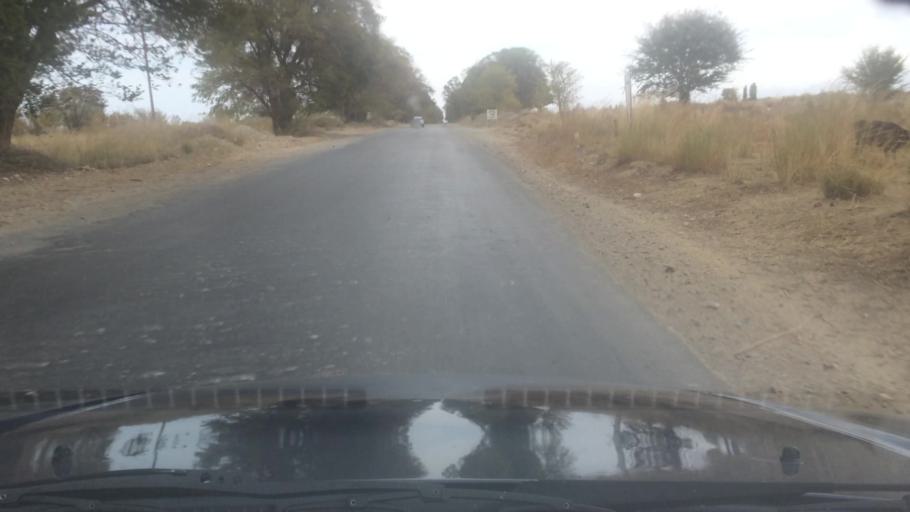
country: KG
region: Ysyk-Koel
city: Balykchy
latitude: 42.3058
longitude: 76.4710
